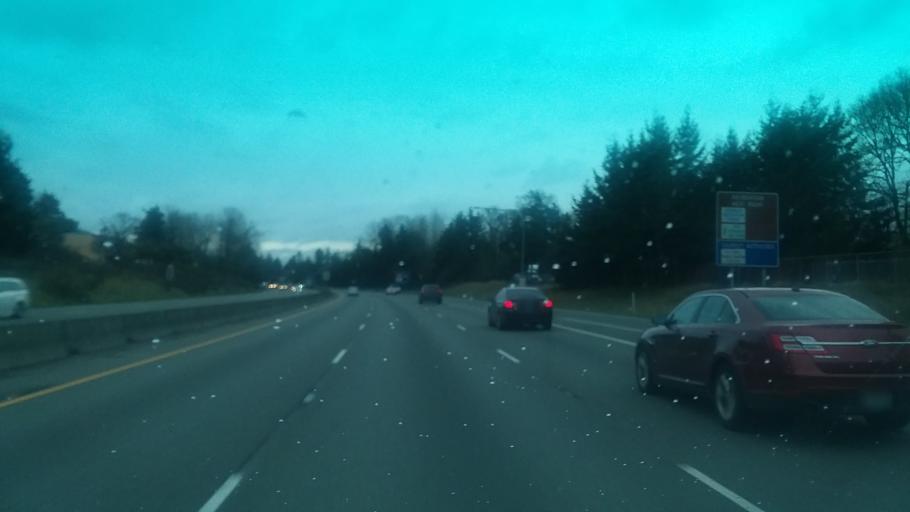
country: US
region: Washington
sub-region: Pierce County
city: Parkland
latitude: 47.1591
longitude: -122.4636
